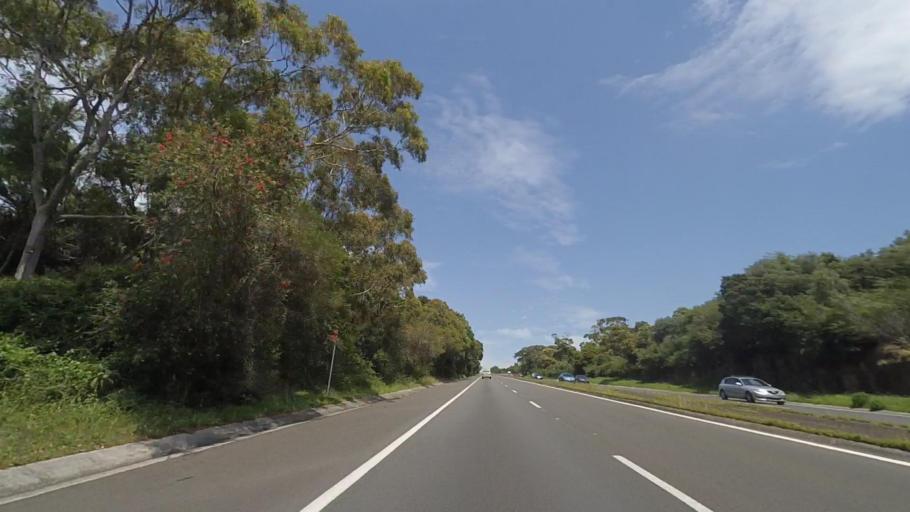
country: AU
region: New South Wales
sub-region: Kiama
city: Kiama
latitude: -34.6690
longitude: 150.8445
